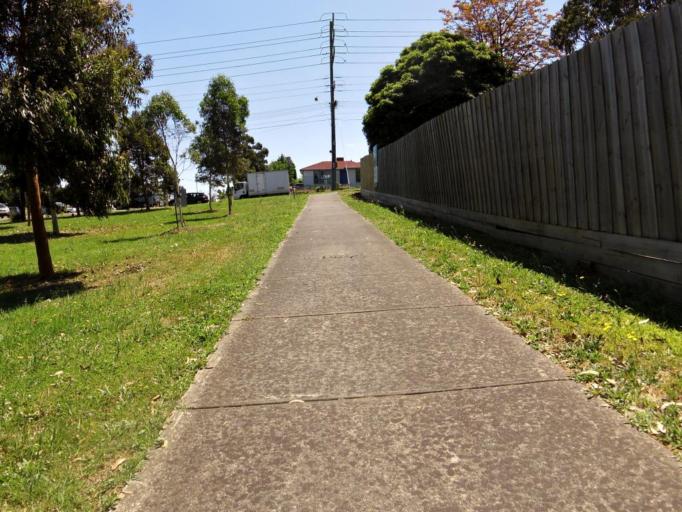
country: AU
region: Victoria
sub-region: Casey
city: Endeavour Hills
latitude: -37.9728
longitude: 145.2430
